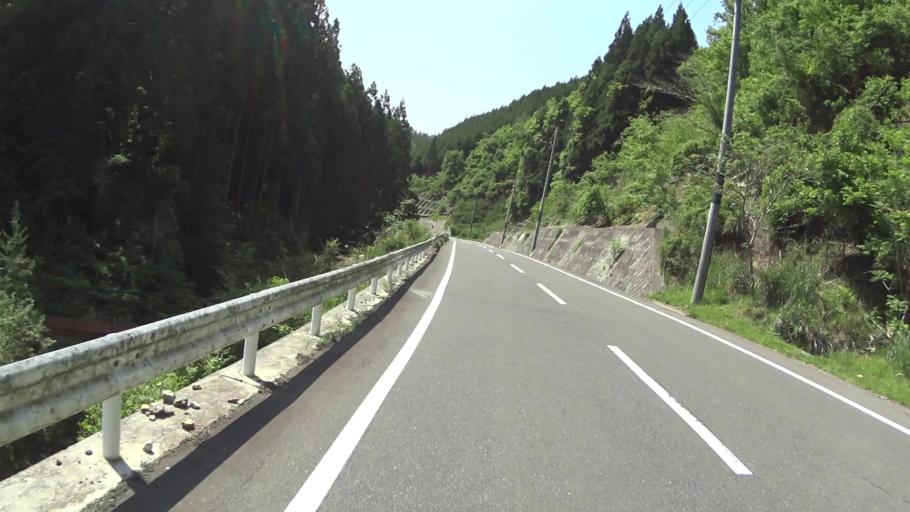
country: JP
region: Kyoto
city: Kameoka
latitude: 35.1205
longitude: 135.5632
